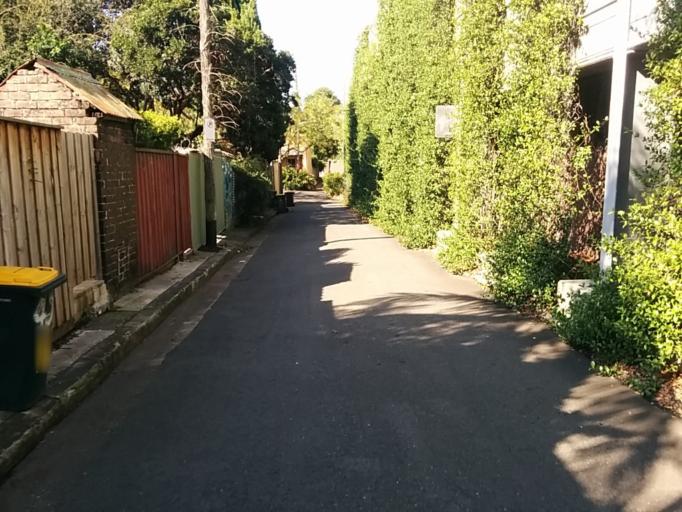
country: AU
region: New South Wales
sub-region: City of Sydney
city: Darlington
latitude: -33.8961
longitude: 151.1873
